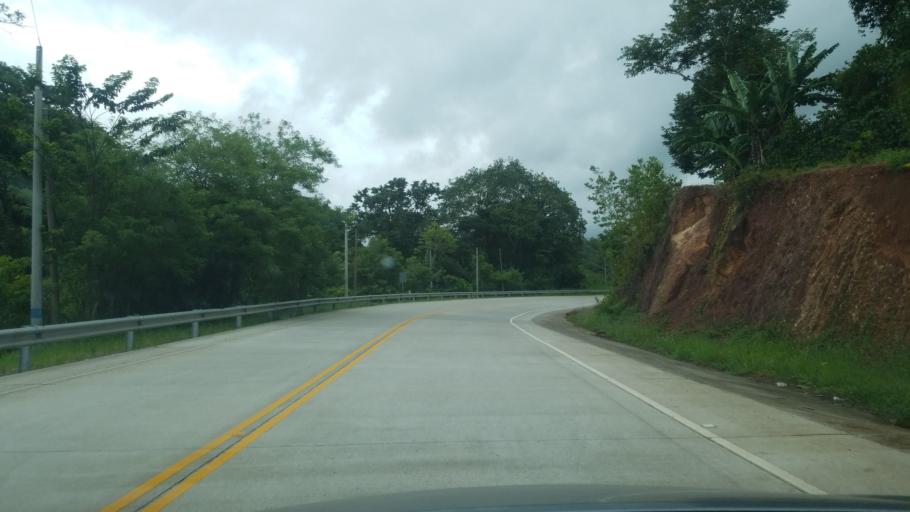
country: HN
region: Copan
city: San Jeronimo
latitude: 14.9456
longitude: -88.9147
